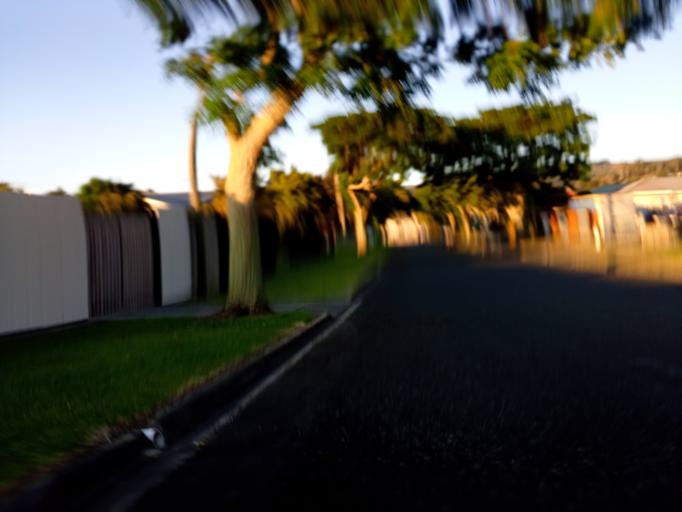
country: NZ
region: Gisborne
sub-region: Gisborne District
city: Gisborne
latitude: -38.6439
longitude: 178.0077
